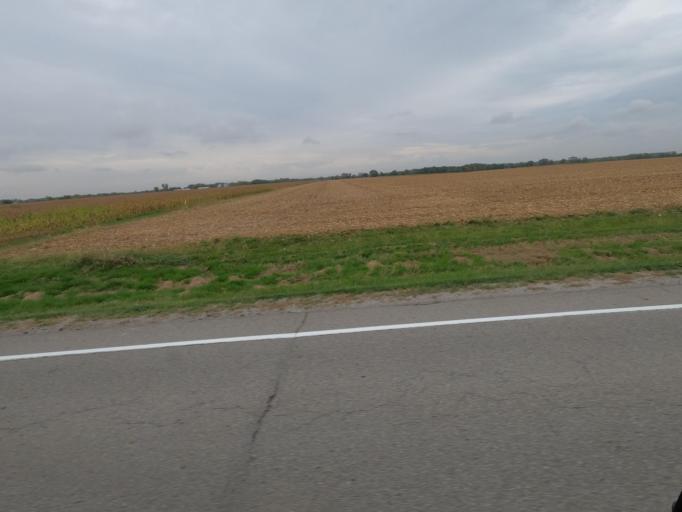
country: US
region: Iowa
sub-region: Van Buren County
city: Keosauqua
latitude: 40.8136
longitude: -91.8862
